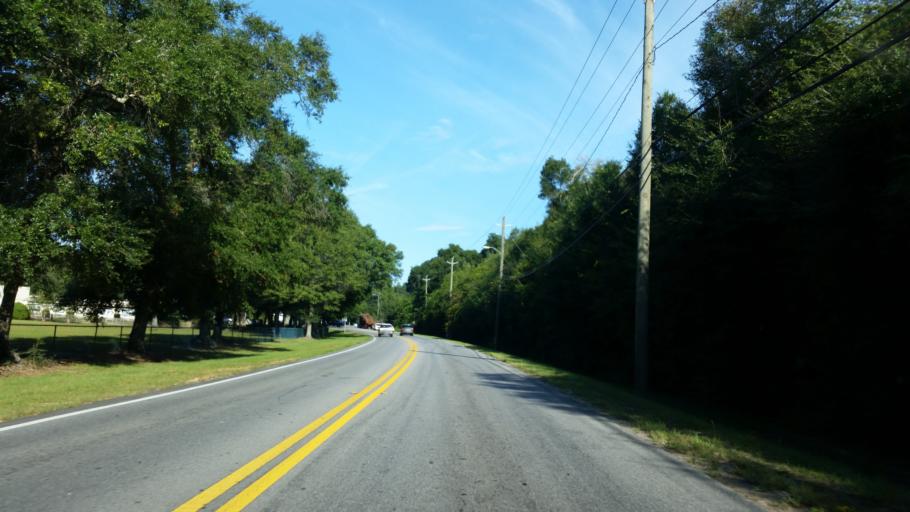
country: US
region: Florida
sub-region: Santa Rosa County
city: Milton
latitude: 30.6300
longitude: -87.0621
